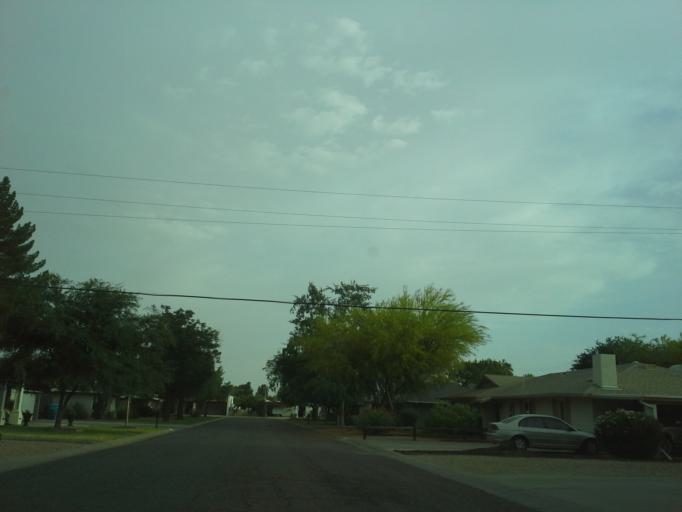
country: US
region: Arizona
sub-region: Maricopa County
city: Phoenix
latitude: 33.5269
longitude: -112.0859
